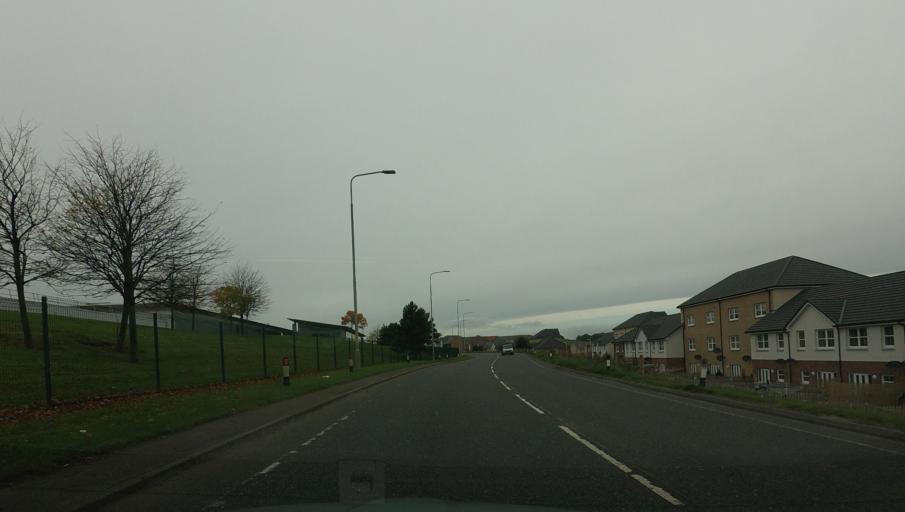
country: GB
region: Scotland
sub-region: Fife
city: Rosyth
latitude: 56.0365
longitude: -3.4323
